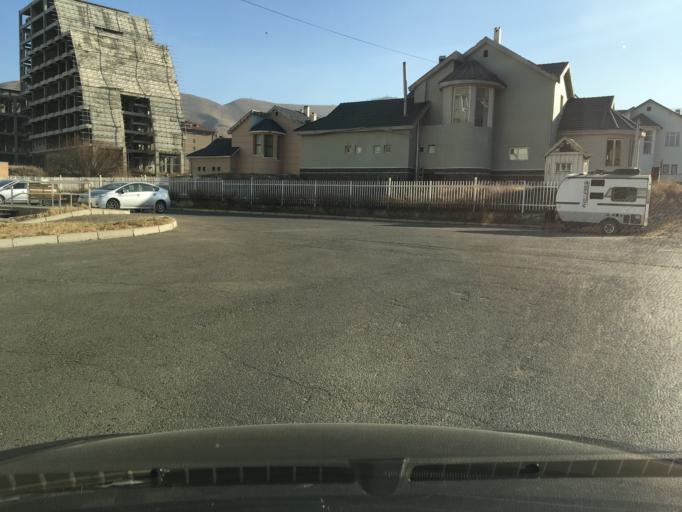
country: MN
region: Ulaanbaatar
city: Ulaanbaatar
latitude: 47.8790
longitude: 106.9095
